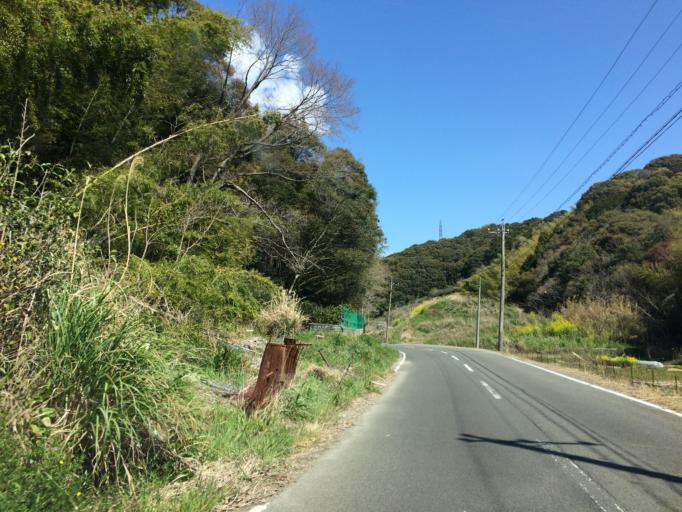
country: JP
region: Shizuoka
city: Fujieda
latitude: 34.8508
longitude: 138.2242
